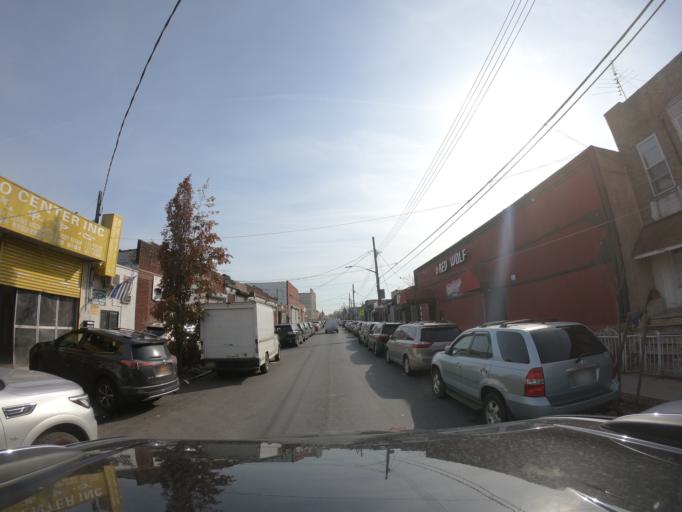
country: US
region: New York
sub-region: Kings County
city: Bensonhurst
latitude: 40.6245
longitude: -73.9943
